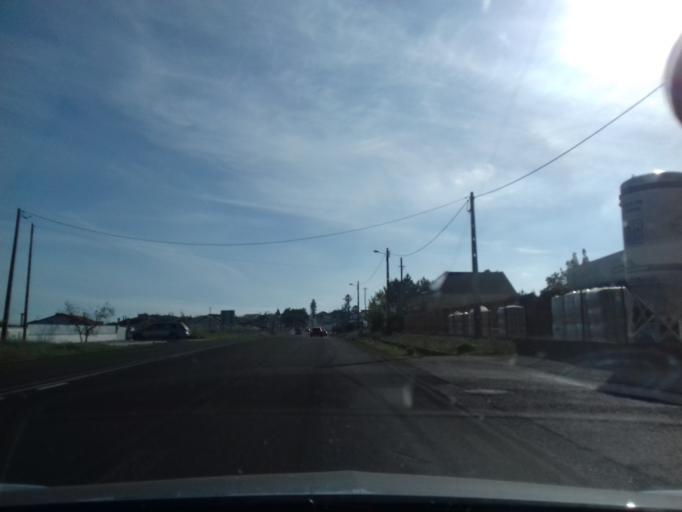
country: PT
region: Leiria
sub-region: Leiria
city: Leiria
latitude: 39.7122
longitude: -8.8404
